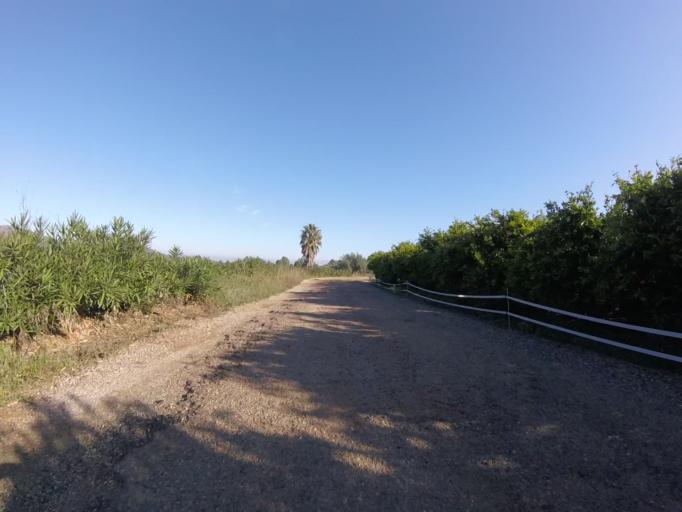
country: ES
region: Valencia
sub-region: Provincia de Castello
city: Santa Magdalena de Pulpis
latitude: 40.3803
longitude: 0.3364
